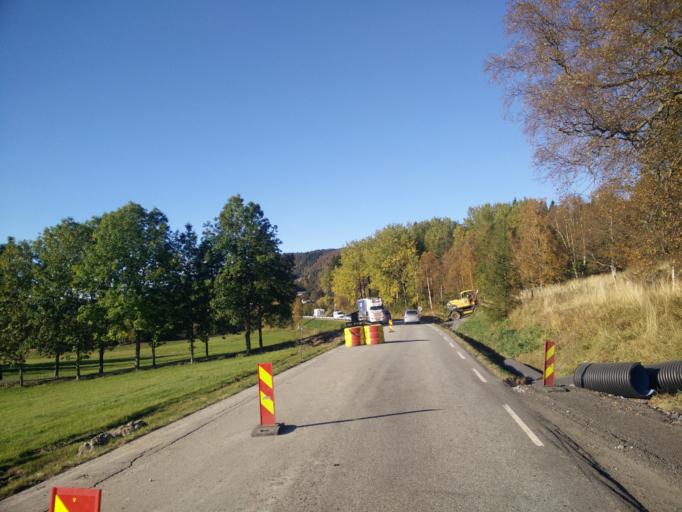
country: NO
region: More og Romsdal
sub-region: Halsa
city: Liaboen
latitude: 63.1124
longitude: 8.3257
